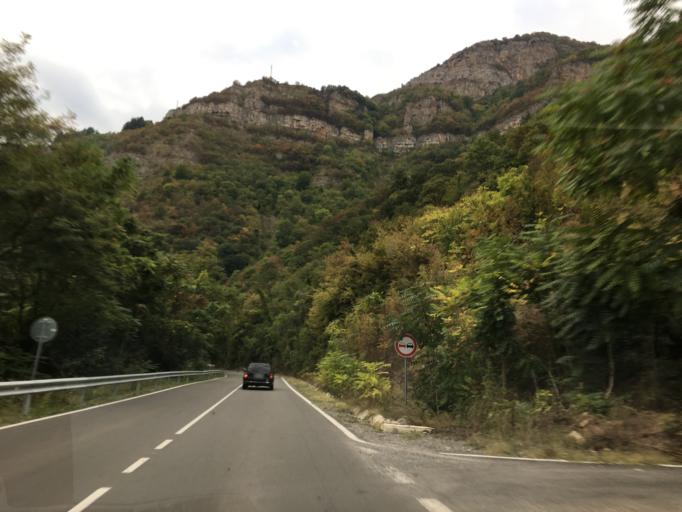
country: BG
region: Sofiya
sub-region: Obshtina Svoge
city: Bov
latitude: 43.0207
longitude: 23.3494
